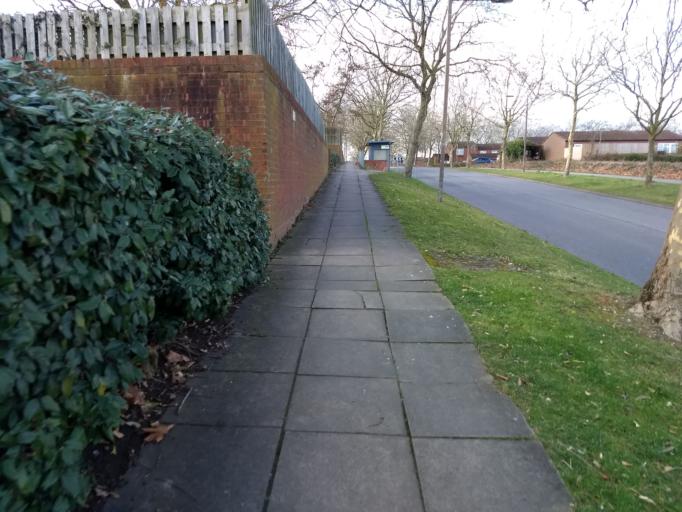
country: GB
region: England
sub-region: Milton Keynes
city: Milton Keynes
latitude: 52.0406
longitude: -0.7362
